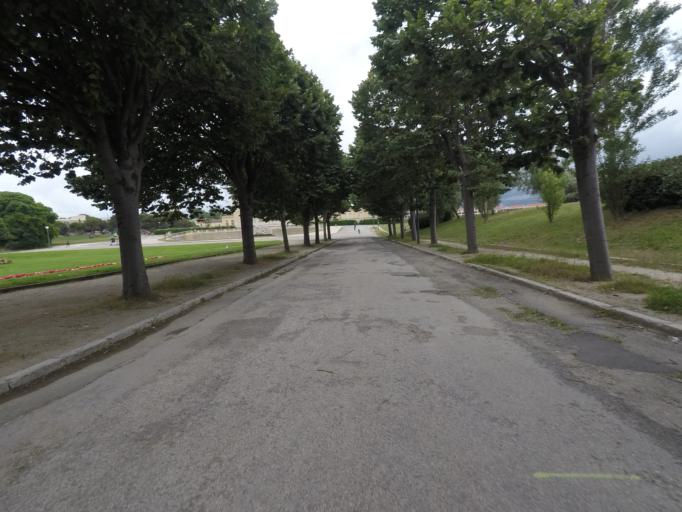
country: FR
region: Provence-Alpes-Cote d'Azur
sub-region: Departement des Bouches-du-Rhone
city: Marseille 08
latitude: 43.2585
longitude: 5.3808
